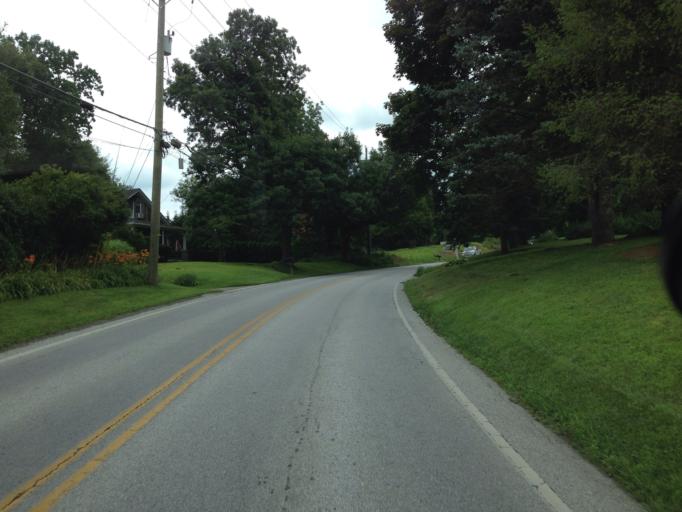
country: US
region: Pennsylvania
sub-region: Chester County
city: West Grove
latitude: 39.8026
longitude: -75.8919
